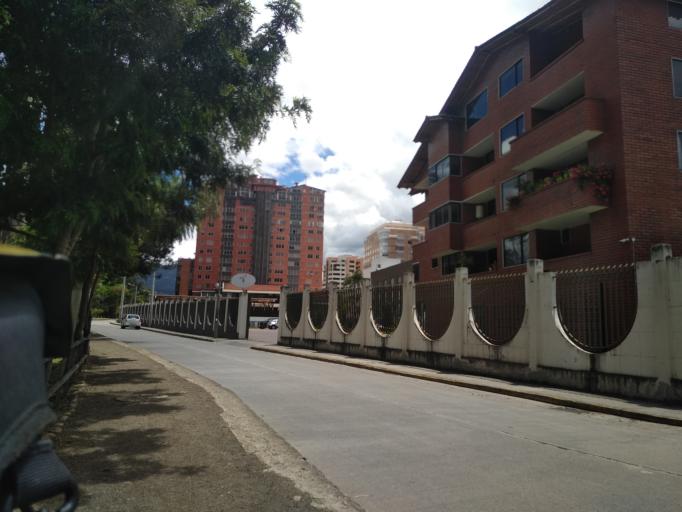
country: EC
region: Azuay
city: Cuenca
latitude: -2.8904
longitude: -79.0308
